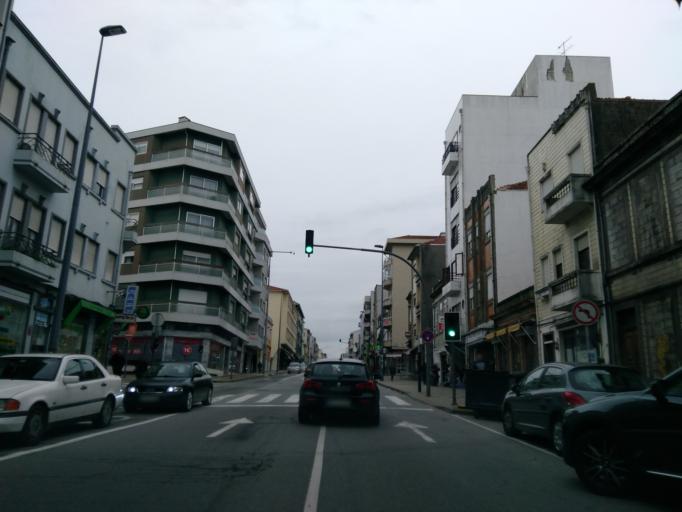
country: PT
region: Porto
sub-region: Porto
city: Porto
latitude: 41.1552
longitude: -8.5953
